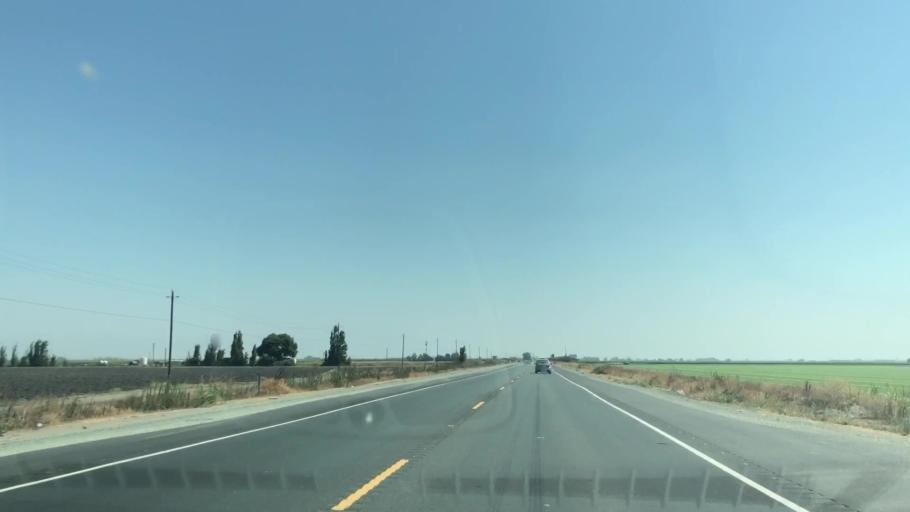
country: US
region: California
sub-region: San Joaquin County
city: Thornton
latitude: 38.1154
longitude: -121.4644
